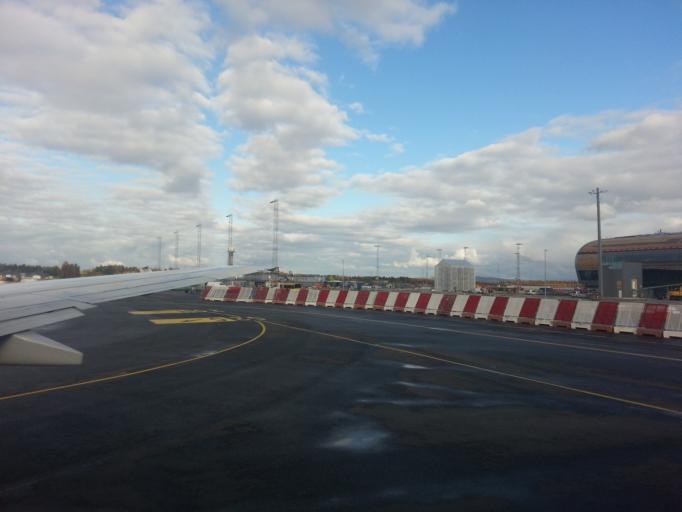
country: NO
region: Akershus
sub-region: Nannestad
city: Teigebyen
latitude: 60.1963
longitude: 11.0970
